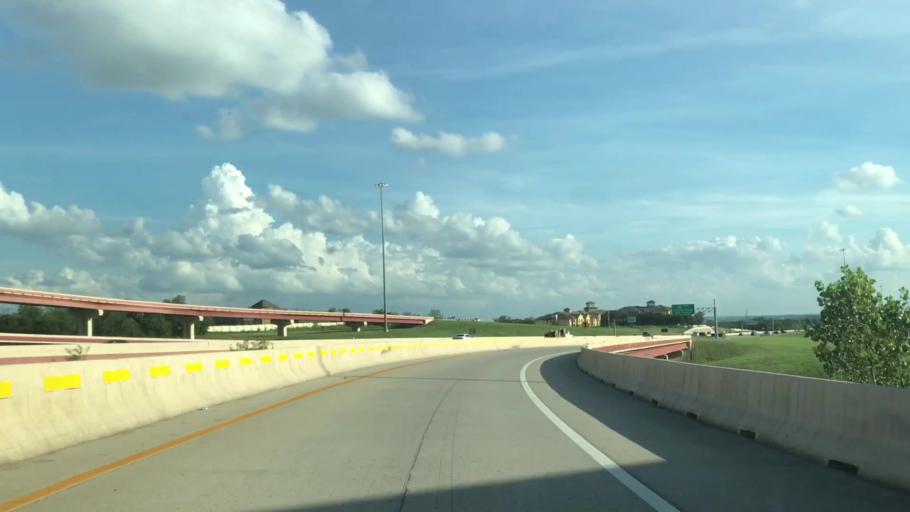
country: US
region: Texas
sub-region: Tarrant County
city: Euless
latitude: 32.8352
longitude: -97.0174
